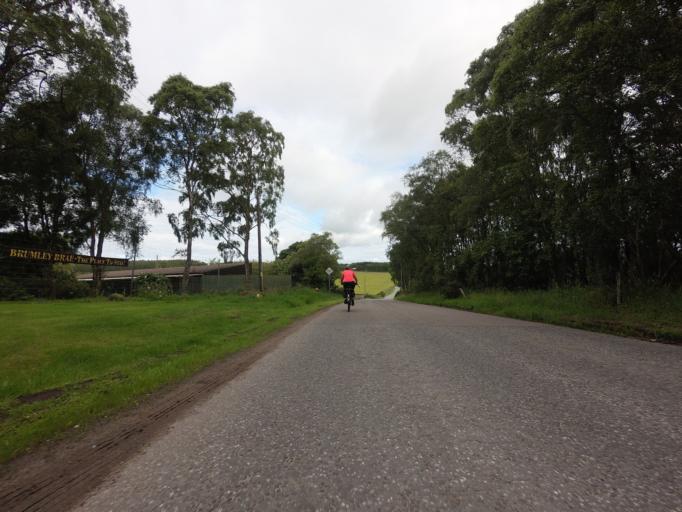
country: GB
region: Scotland
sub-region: Moray
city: Elgin
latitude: 57.6558
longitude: -3.3493
